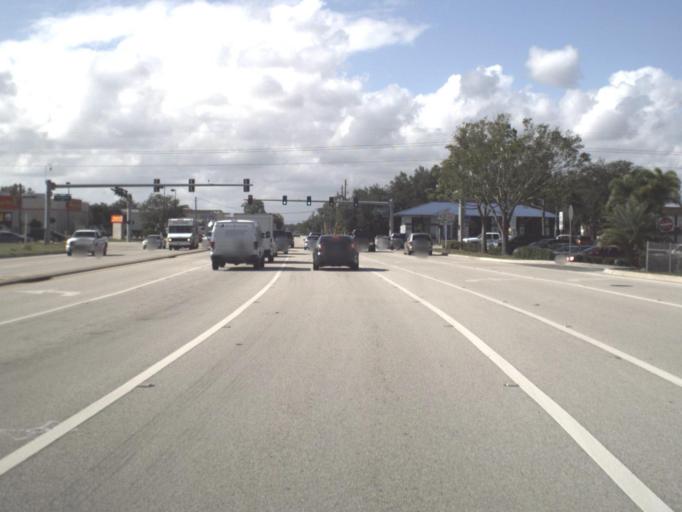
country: US
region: Florida
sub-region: Brevard County
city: June Park
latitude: 28.0998
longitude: -80.6714
